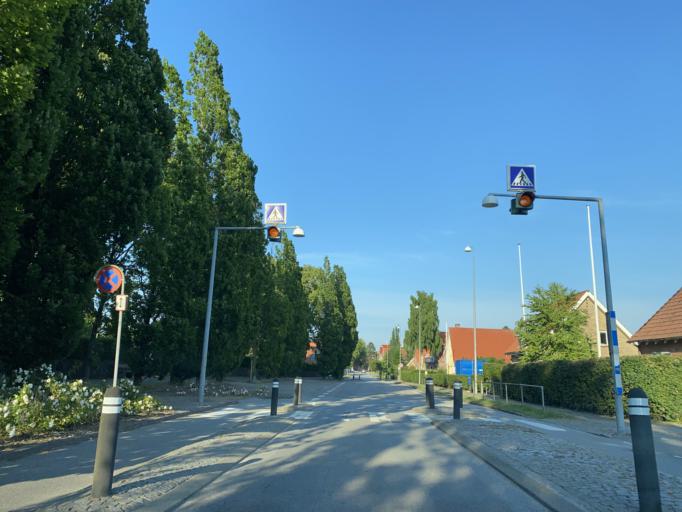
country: DK
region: South Denmark
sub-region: Aabenraa Kommune
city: Aabenraa
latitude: 55.0449
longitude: 9.4066
